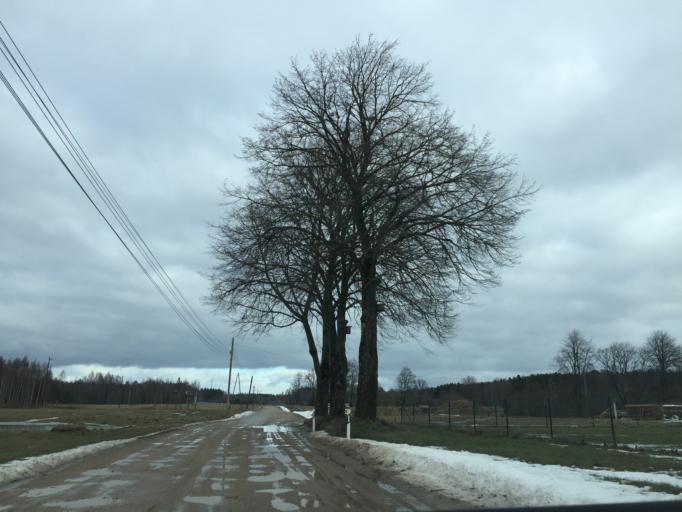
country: LV
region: Salacgrivas
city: Ainazi
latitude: 57.8499
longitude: 24.4859
